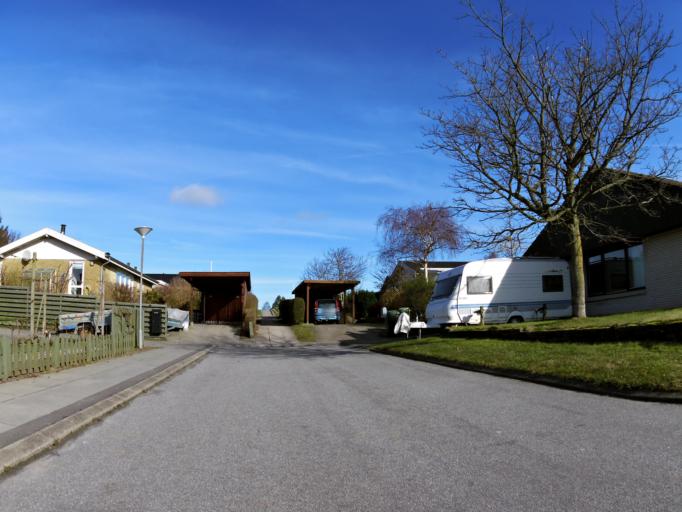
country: DK
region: Central Jutland
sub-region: Arhus Kommune
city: Tranbjerg
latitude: 56.0887
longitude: 10.1169
